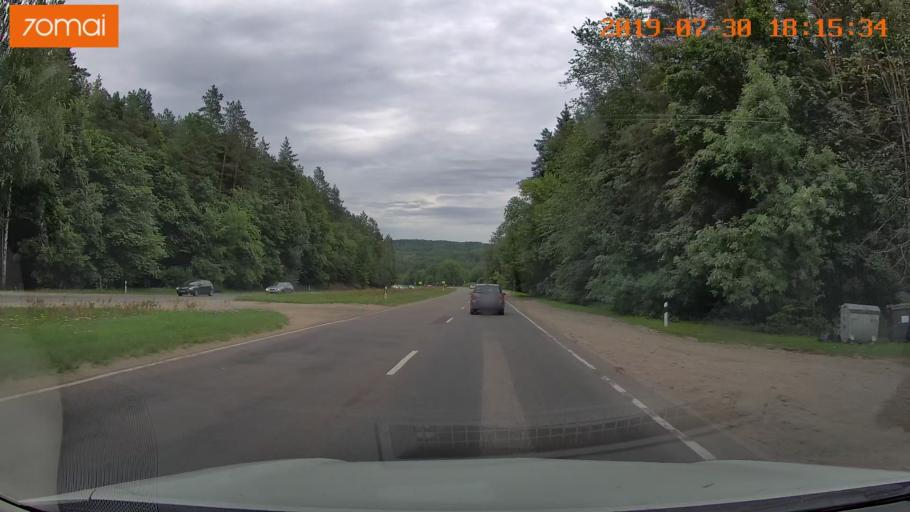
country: LT
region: Vilnius County
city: Rasos
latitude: 54.6930
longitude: 25.3535
